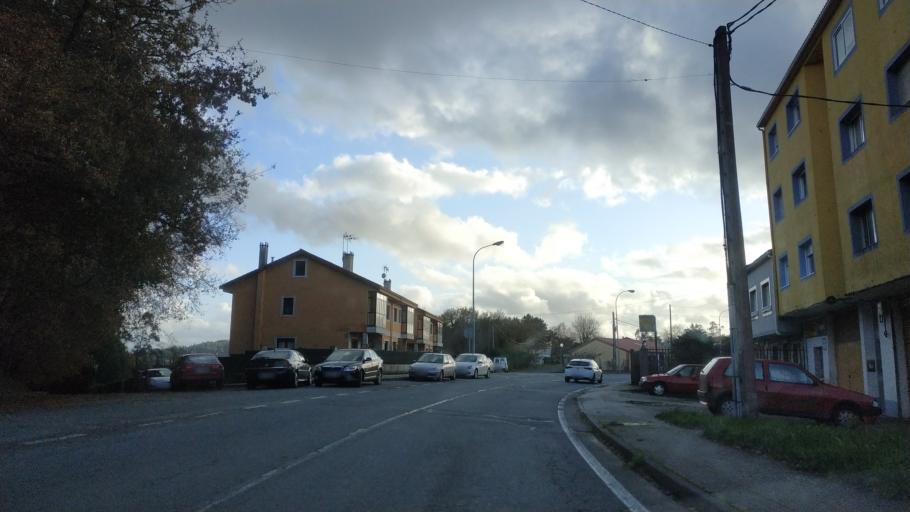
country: ES
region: Galicia
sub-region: Provincia da Coruna
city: Arzua
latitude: 42.9196
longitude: -8.1652
